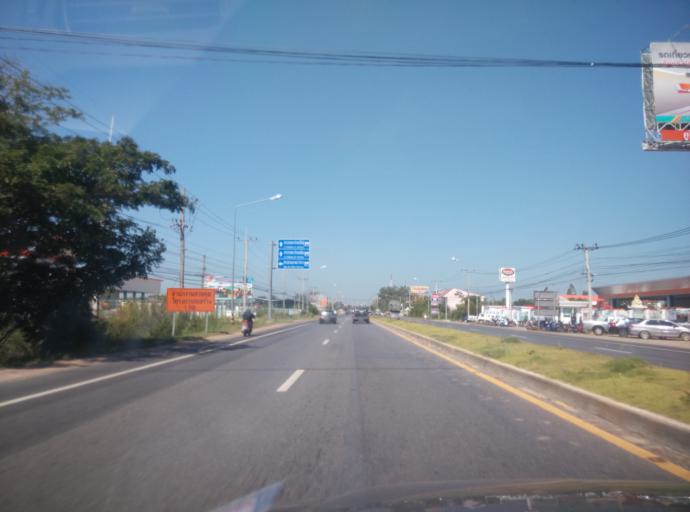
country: TH
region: Sisaket
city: Si Sa Ket
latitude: 15.1254
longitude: 104.2898
